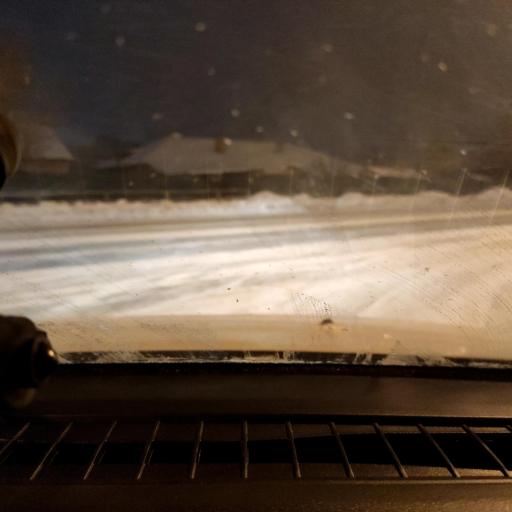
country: RU
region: Samara
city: Otradnyy
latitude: 53.3578
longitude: 51.3424
